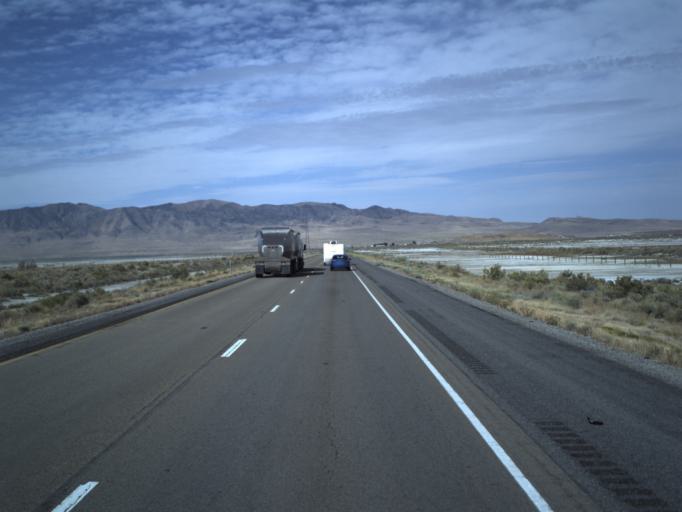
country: US
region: Utah
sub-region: Tooele County
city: Grantsville
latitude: 40.7557
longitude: -112.7484
